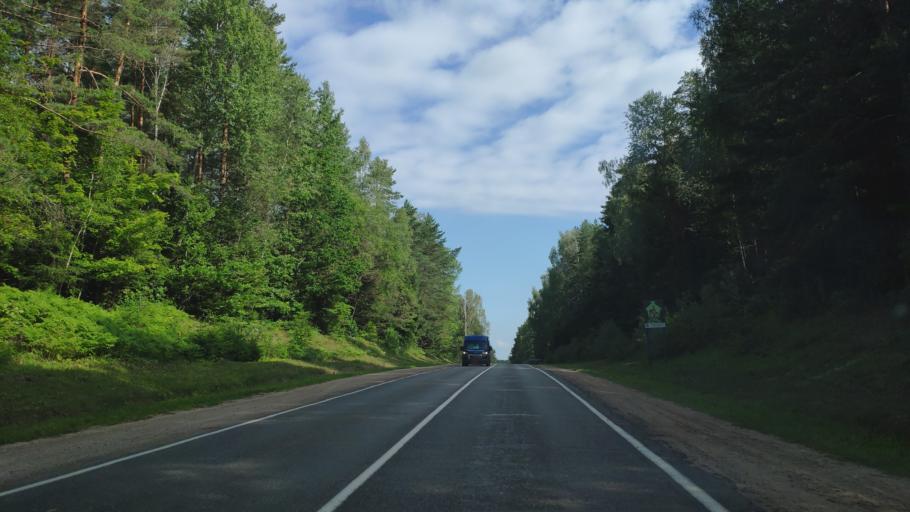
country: BY
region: Minsk
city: Novosel'ye
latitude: 53.9427
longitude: 27.2448
